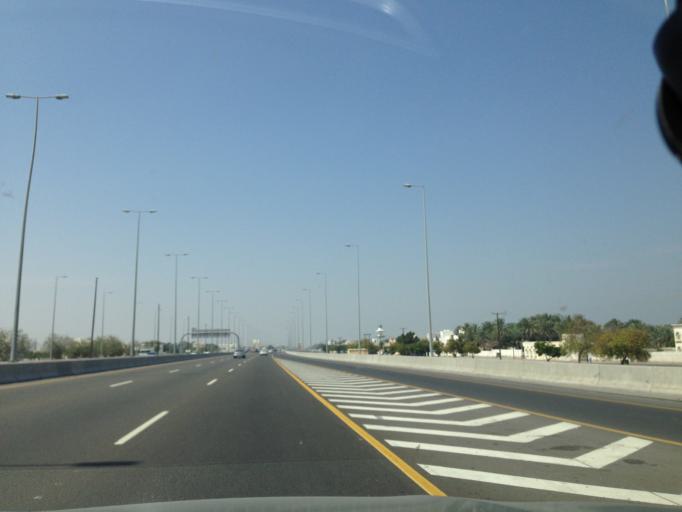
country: OM
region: Muhafazat Masqat
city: As Sib al Jadidah
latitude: 23.6663
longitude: 58.1590
